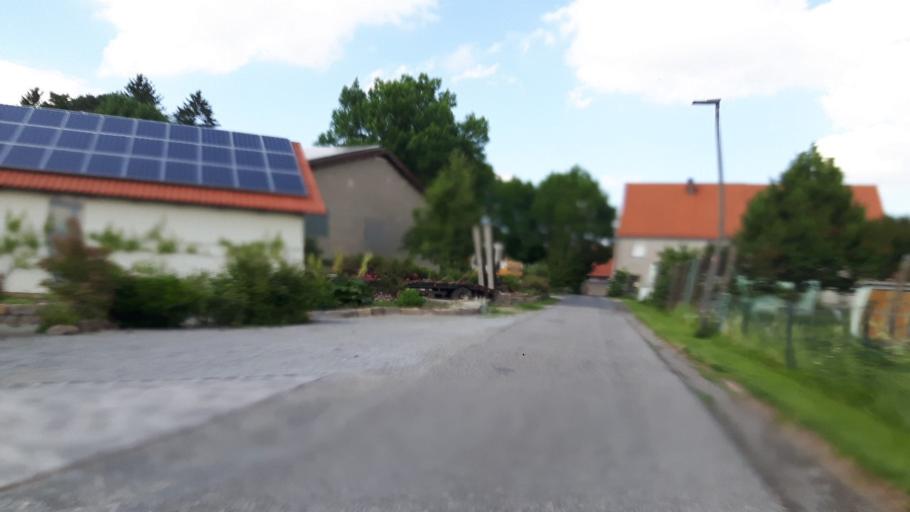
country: DE
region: Bavaria
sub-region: Regierungsbezirk Unterfranken
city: Geroldshausen
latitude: 49.6830
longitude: 9.8992
